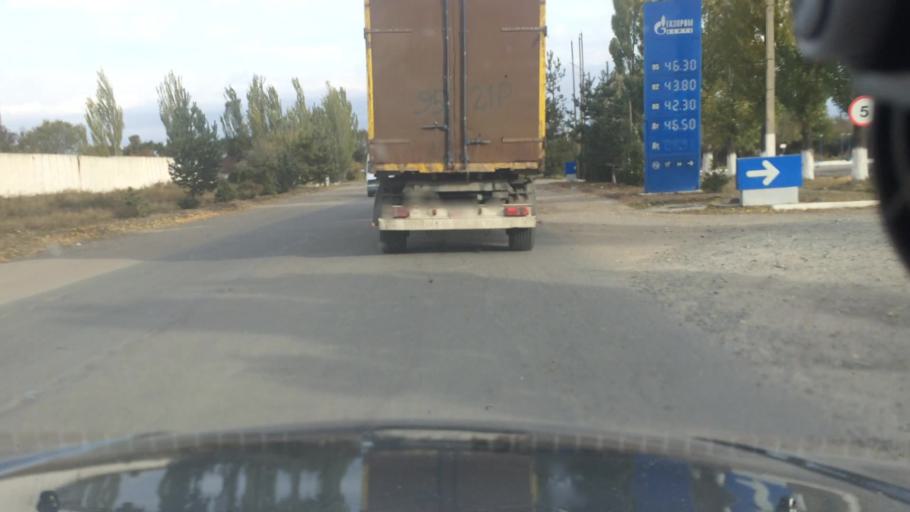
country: KG
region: Ysyk-Koel
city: Karakol
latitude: 42.5160
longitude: 78.3858
